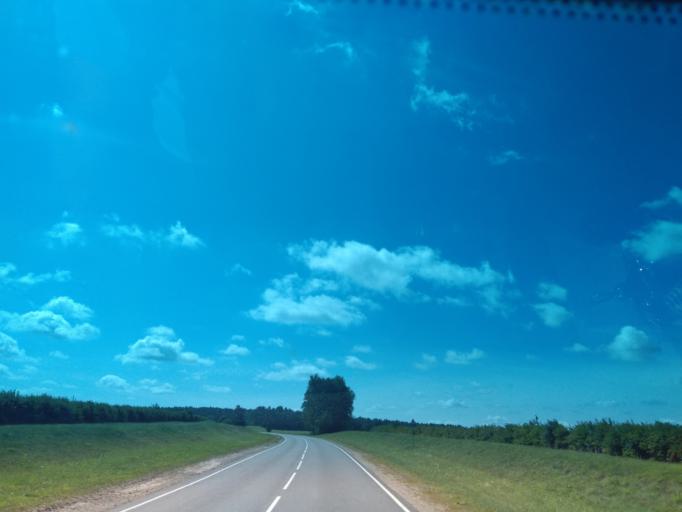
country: BY
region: Minsk
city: Uzda
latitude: 53.3621
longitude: 27.2256
